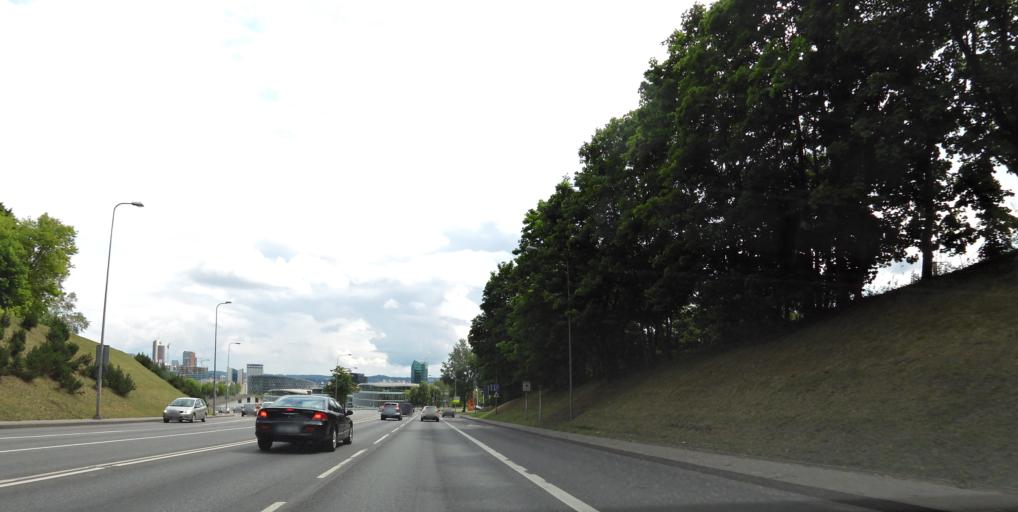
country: LT
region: Vilnius County
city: Seskine
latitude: 54.7045
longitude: 25.2568
